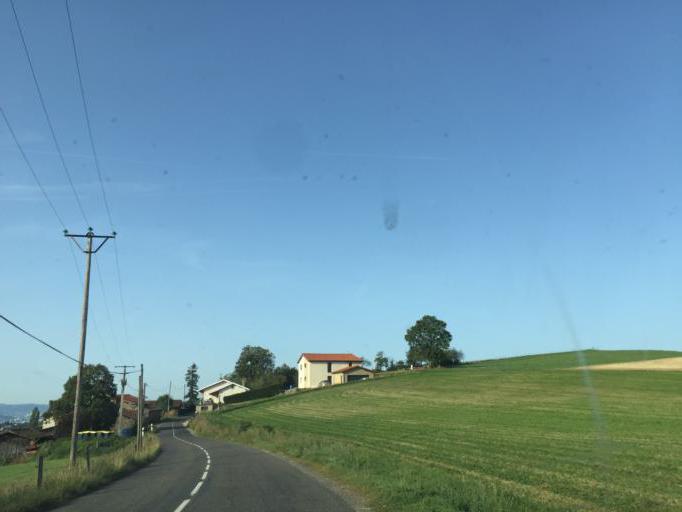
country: FR
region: Rhone-Alpes
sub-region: Departement de la Loire
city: Saint-Christo-en-Jarez
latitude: 45.5213
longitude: 4.4658
